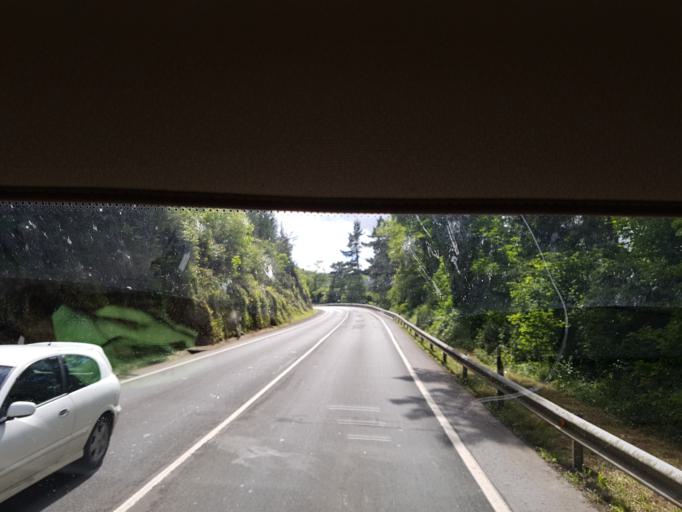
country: ES
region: Basque Country
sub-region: Bizkaia
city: Sopuerta
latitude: 43.2759
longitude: -3.1451
